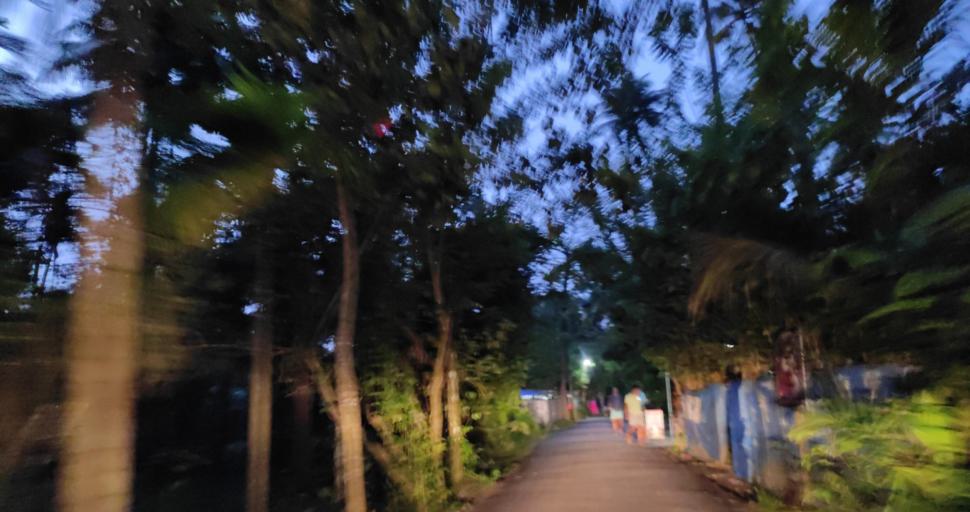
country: IN
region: Kerala
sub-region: Alappuzha
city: Vayalar
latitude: 9.7236
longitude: 76.2911
